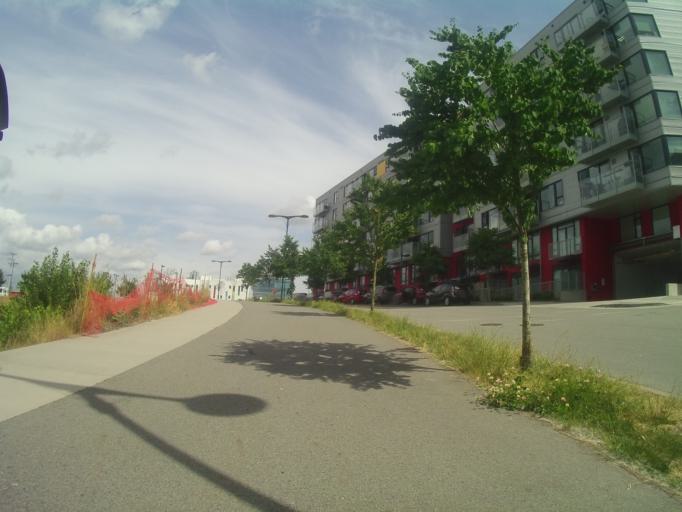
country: CA
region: British Columbia
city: Vancouver
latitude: 49.2678
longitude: -123.0961
